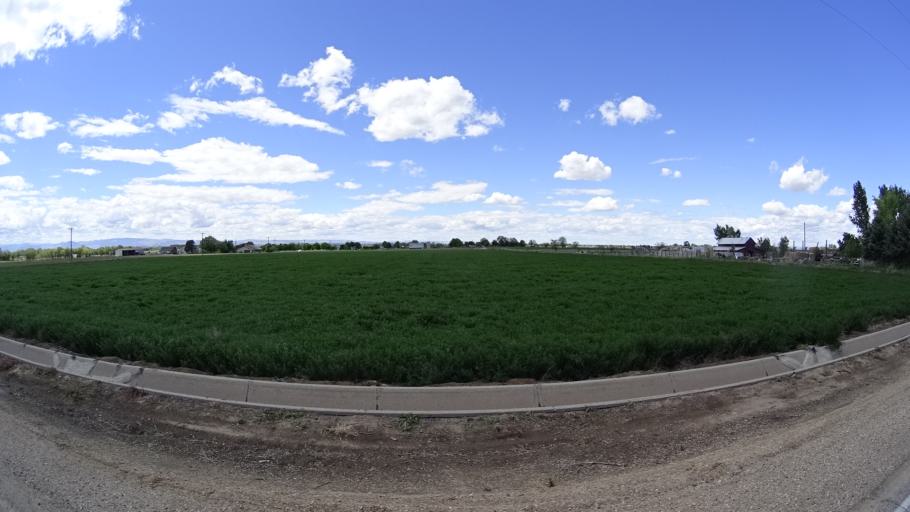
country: US
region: Idaho
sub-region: Ada County
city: Kuna
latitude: 43.5475
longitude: -116.4537
